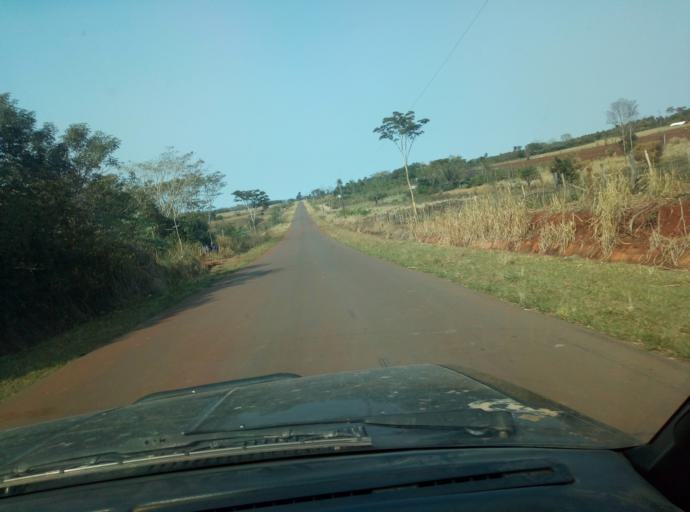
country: PY
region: Caaguazu
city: Carayao
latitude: -25.2234
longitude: -56.2890
